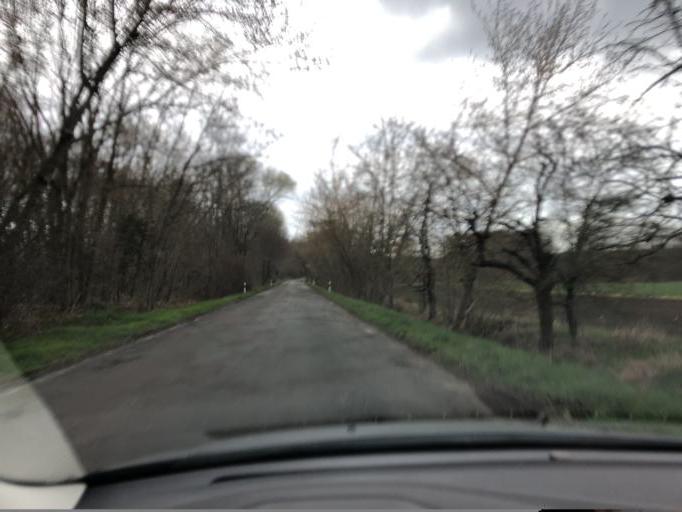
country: DE
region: Saxony-Anhalt
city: Muschwitz
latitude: 51.1803
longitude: 12.1336
